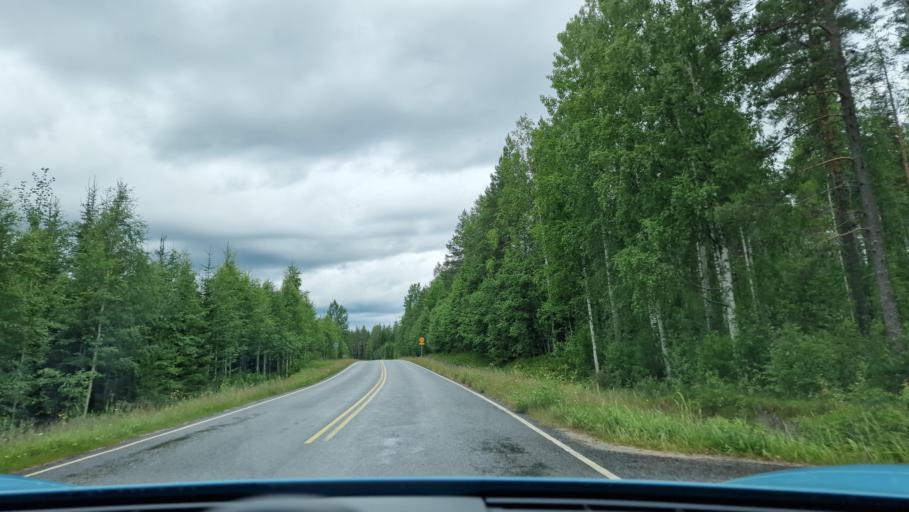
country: FI
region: Southern Ostrobothnia
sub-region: Jaerviseutu
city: Soini
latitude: 62.7032
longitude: 24.4530
